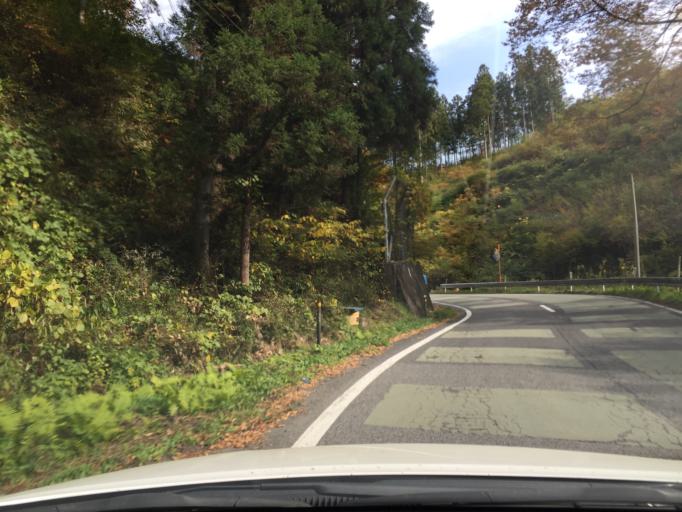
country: JP
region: Fukushima
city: Ishikawa
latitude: 36.9780
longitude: 140.4562
